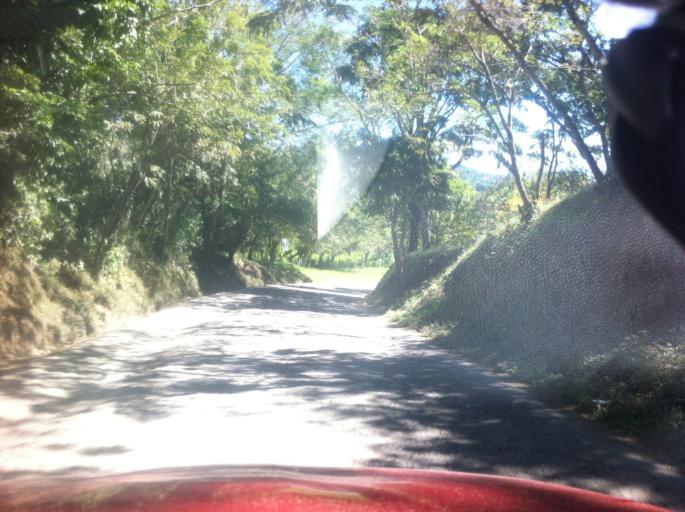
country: NI
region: Matagalpa
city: San Ramon
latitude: 12.9409
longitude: -85.8739
